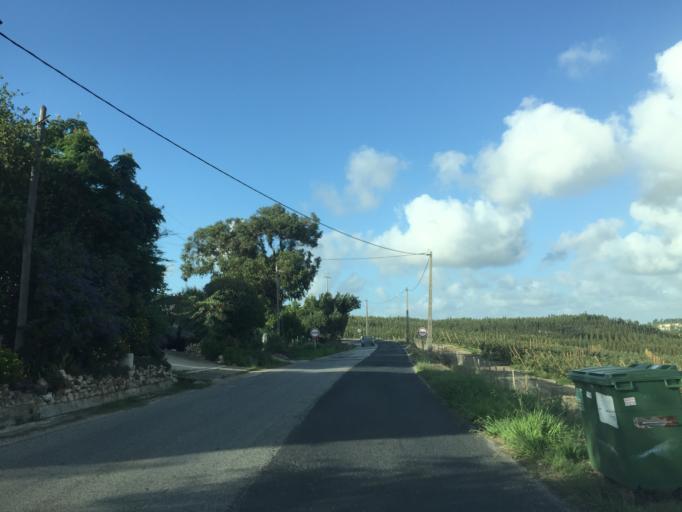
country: PT
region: Lisbon
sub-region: Torres Vedras
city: Torres Vedras
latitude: 39.1195
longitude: -9.2632
